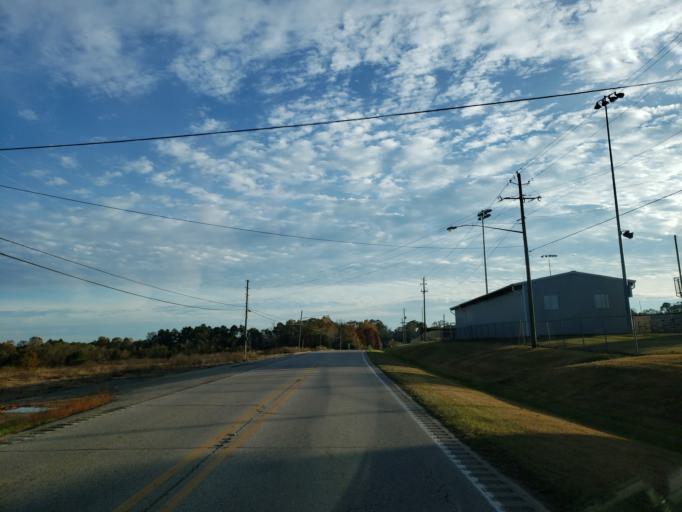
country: US
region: Mississippi
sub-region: Lamar County
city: Purvis
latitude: 31.1382
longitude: -89.4055
